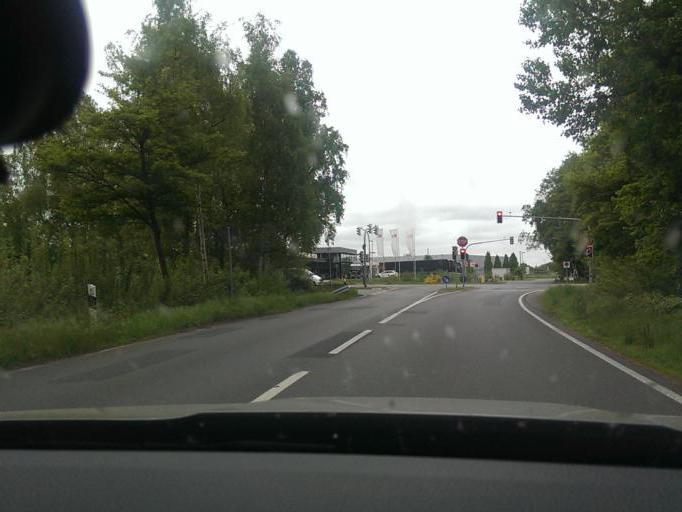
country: DE
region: Lower Saxony
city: Langenhagen
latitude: 52.4594
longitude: 9.7156
